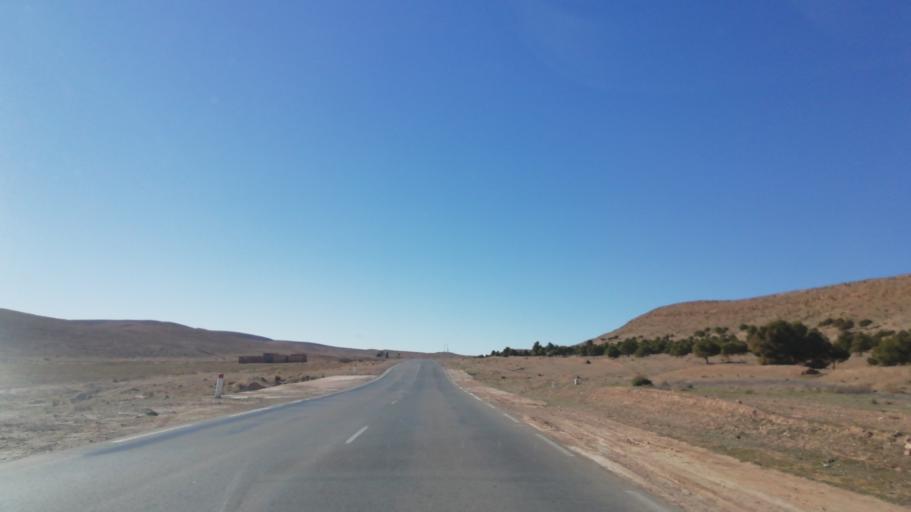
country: DZ
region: El Bayadh
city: El Bayadh
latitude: 33.6798
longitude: 1.4520
